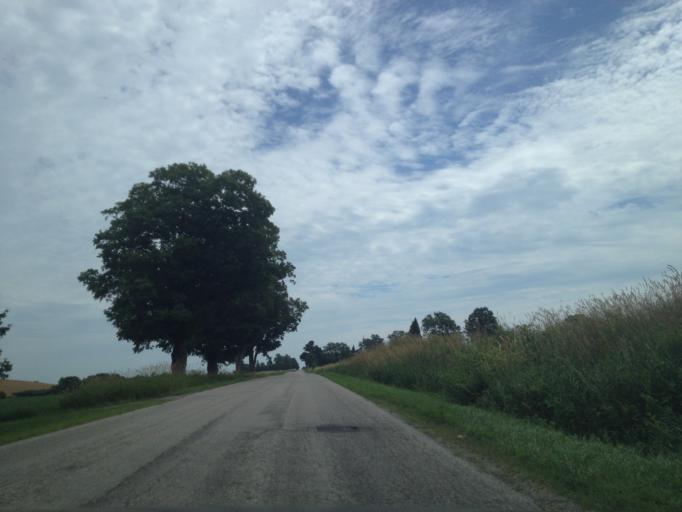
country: CA
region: Ontario
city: Ingersoll
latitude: 42.9771
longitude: -80.7671
